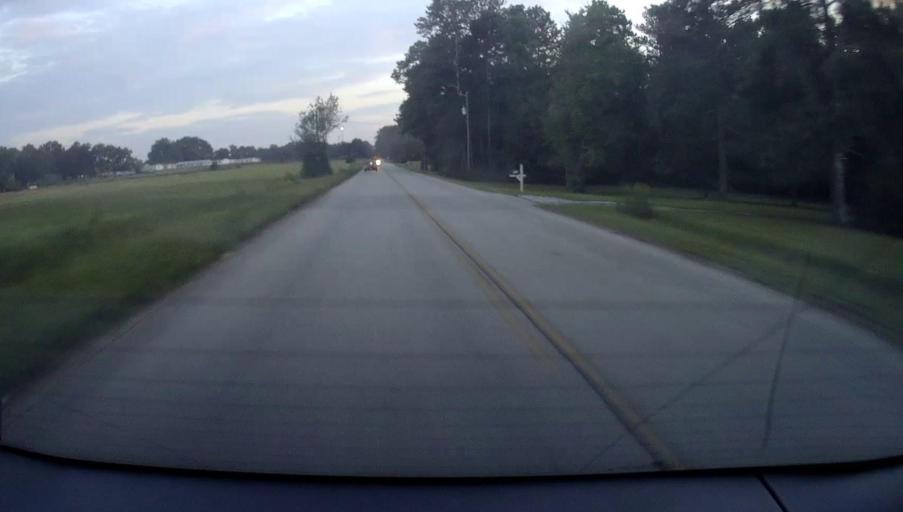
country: US
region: Georgia
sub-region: Butts County
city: Jackson
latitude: 33.3047
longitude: -84.0430
